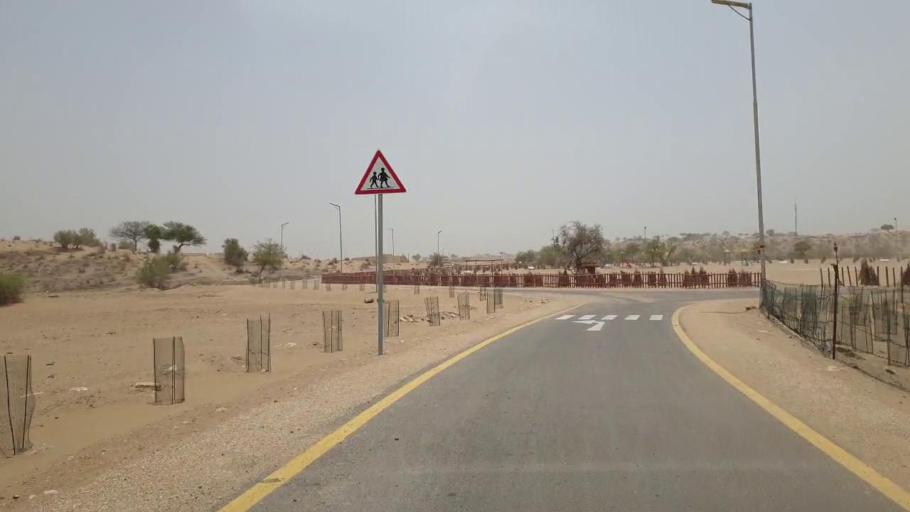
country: PK
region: Sindh
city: Islamkot
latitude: 24.7257
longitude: 70.3240
